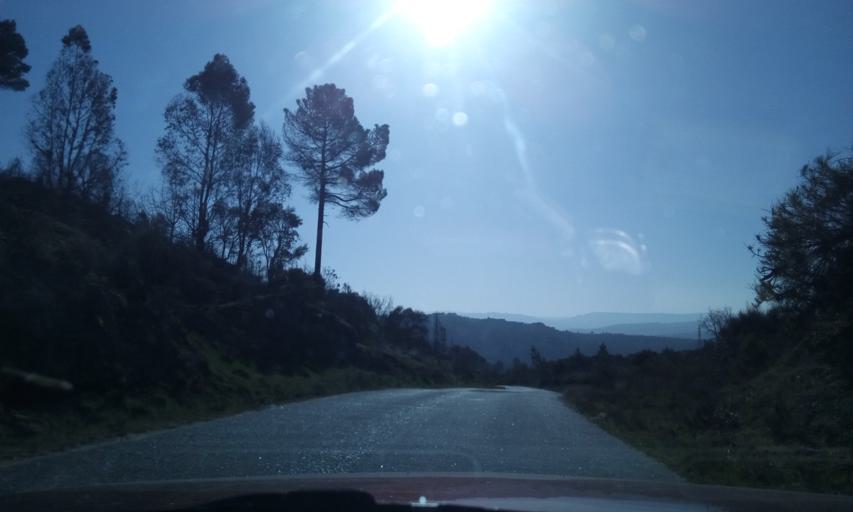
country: PT
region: Guarda
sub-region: Celorico da Beira
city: Celorico da Beira
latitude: 40.6890
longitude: -7.4185
